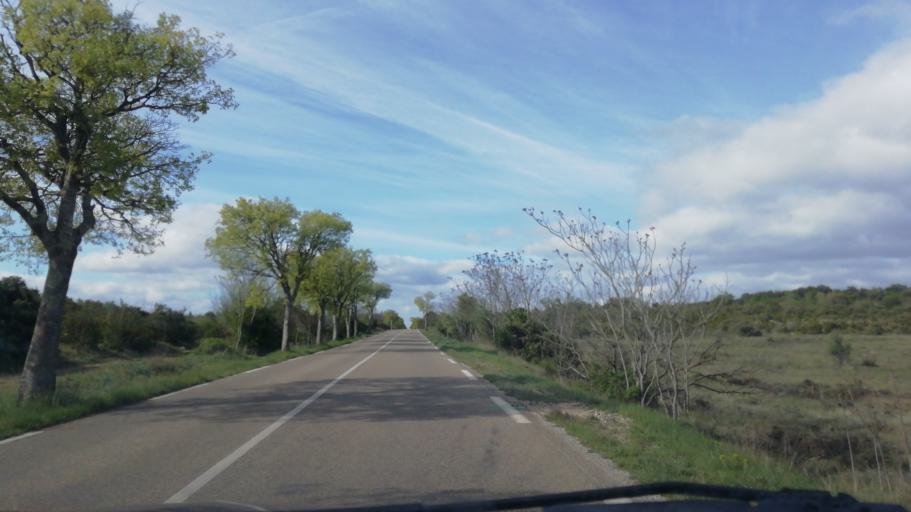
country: FR
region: Languedoc-Roussillon
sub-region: Departement de l'Herault
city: Saint-Martin-de-Londres
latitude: 43.7687
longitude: 3.7252
